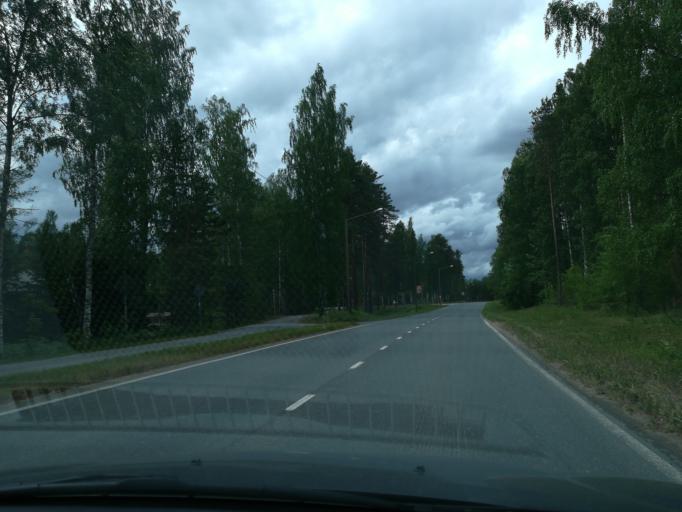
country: FI
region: South Karelia
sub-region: Lappeenranta
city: Savitaipale
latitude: 61.1954
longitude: 27.7021
